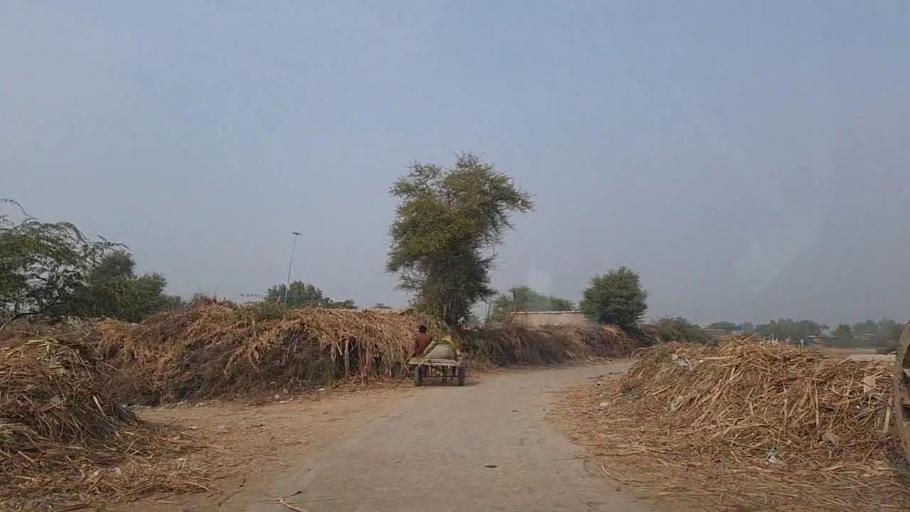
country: PK
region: Sindh
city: Sanghar
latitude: 26.0855
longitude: 68.8964
